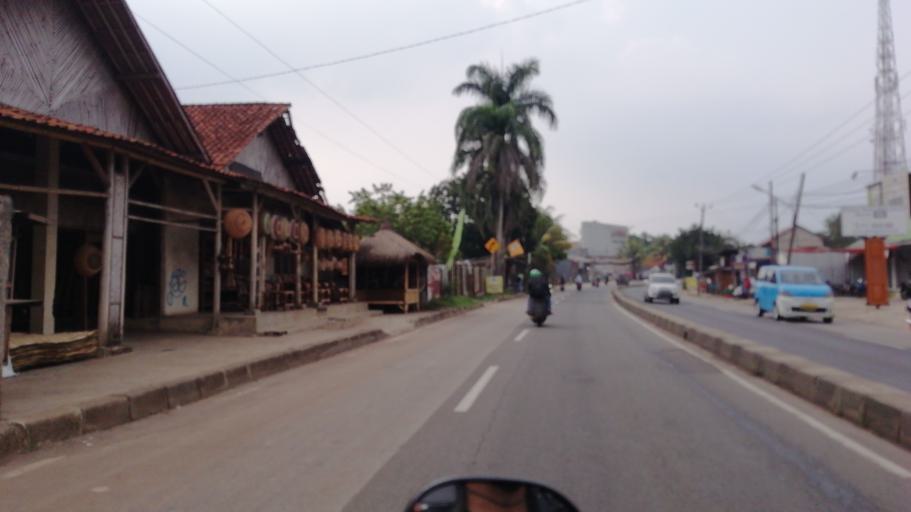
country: ID
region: West Java
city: Parung
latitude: -6.4836
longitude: 106.7325
